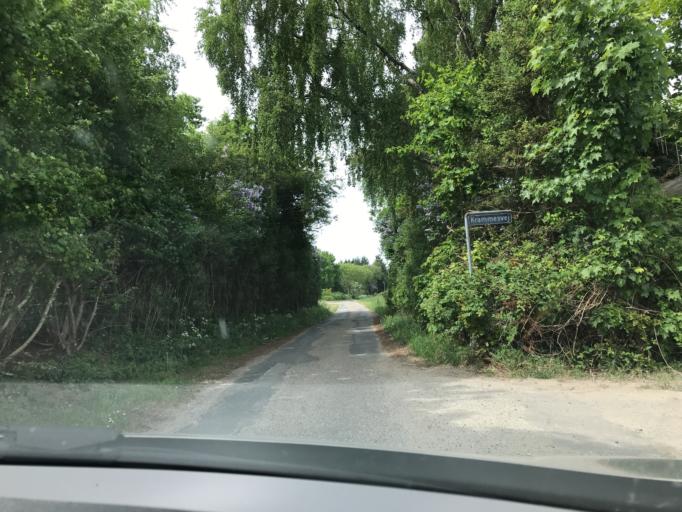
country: DK
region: Central Jutland
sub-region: Norddjurs Kommune
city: Allingabro
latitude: 56.5947
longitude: 10.3176
